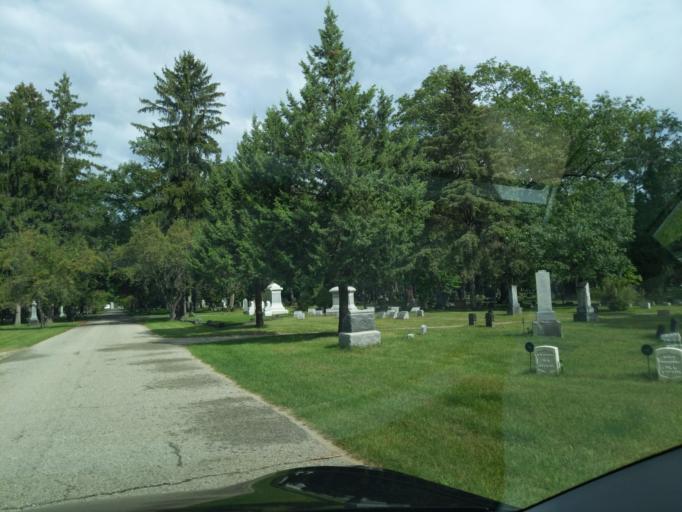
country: US
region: Michigan
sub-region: Grand Traverse County
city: Traverse City
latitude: 44.7558
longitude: -85.5891
